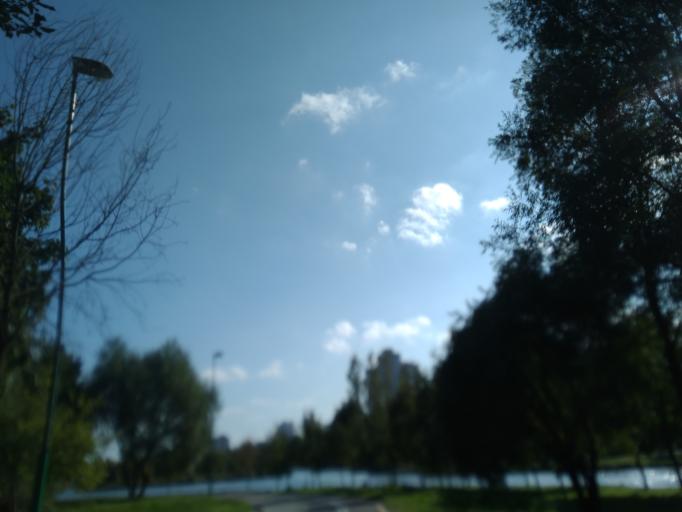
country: BY
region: Minsk
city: Minsk
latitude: 53.8833
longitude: 27.5737
